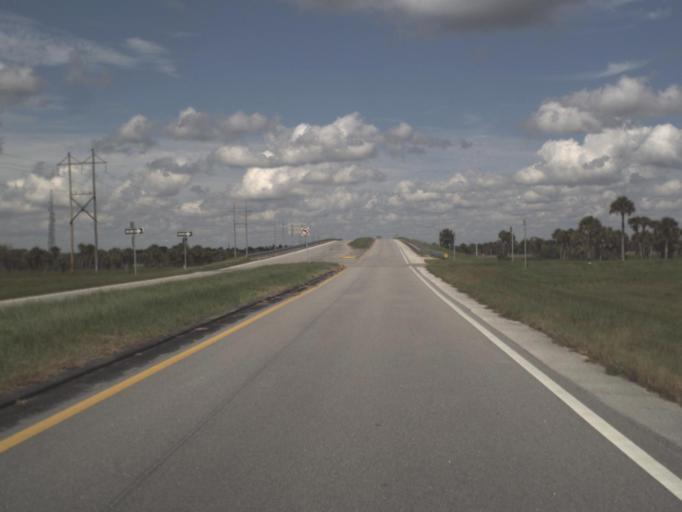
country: US
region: Florida
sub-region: Collier County
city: Immokalee
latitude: 26.1510
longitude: -81.3450
